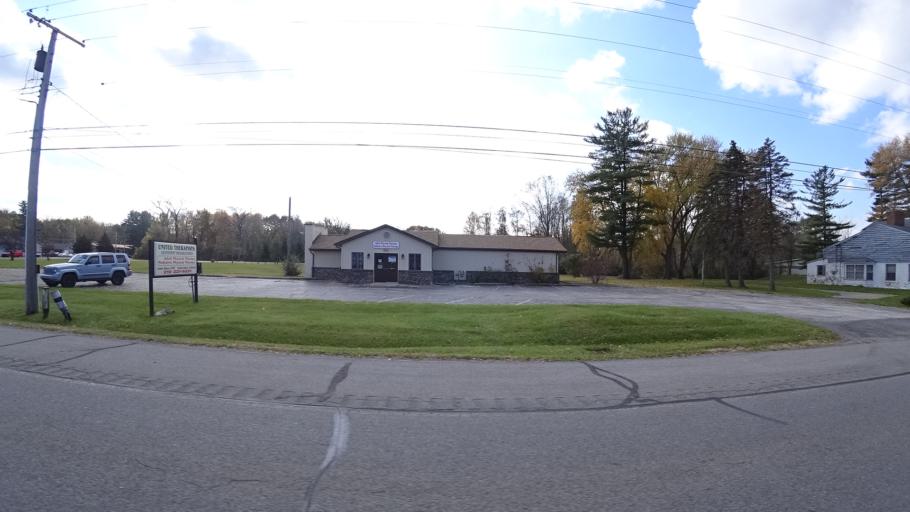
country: US
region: Indiana
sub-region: LaPorte County
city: Trail Creek
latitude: 41.7041
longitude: -86.8515
